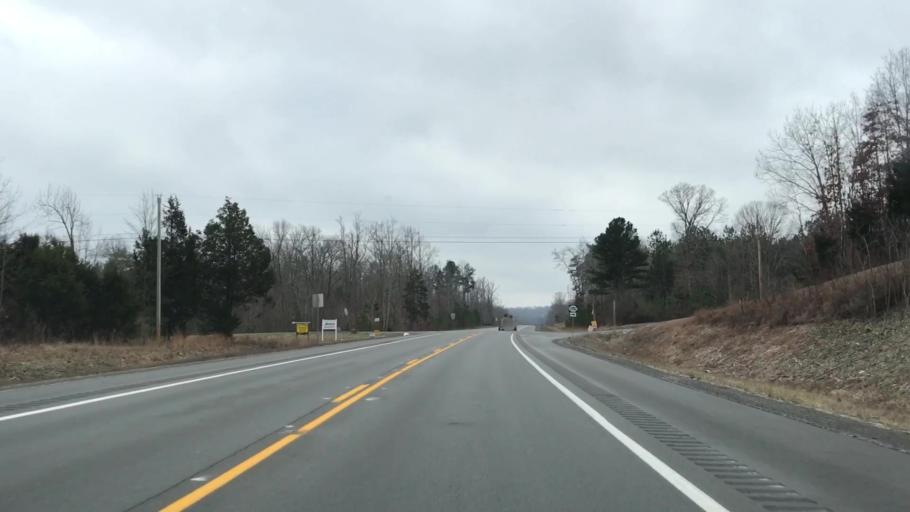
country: US
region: Kentucky
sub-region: Adair County
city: Columbia
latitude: 37.0497
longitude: -85.3632
